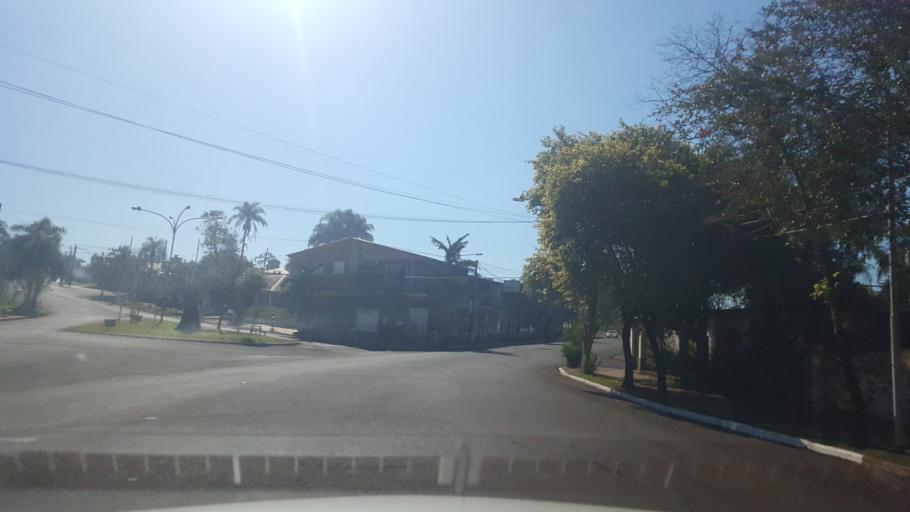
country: AR
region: Misiones
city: Puerto Rico
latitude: -26.8054
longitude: -55.0239
